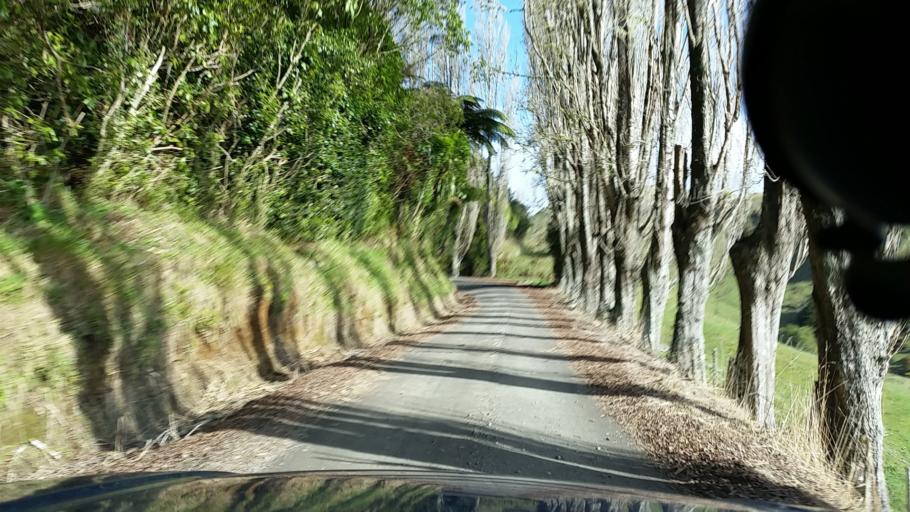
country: NZ
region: Taranaki
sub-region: New Plymouth District
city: Waitara
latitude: -39.0319
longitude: 174.7902
